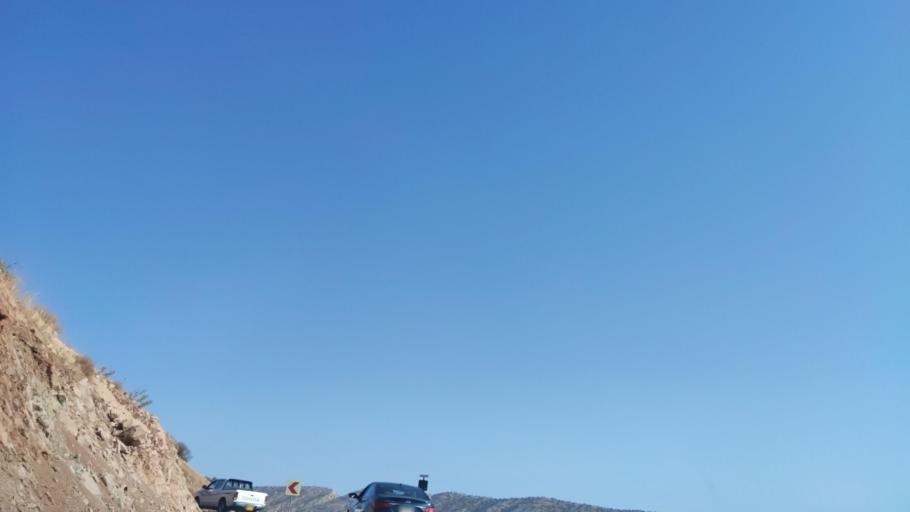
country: IQ
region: Arbil
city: Shaqlawah
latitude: 36.4341
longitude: 44.3008
